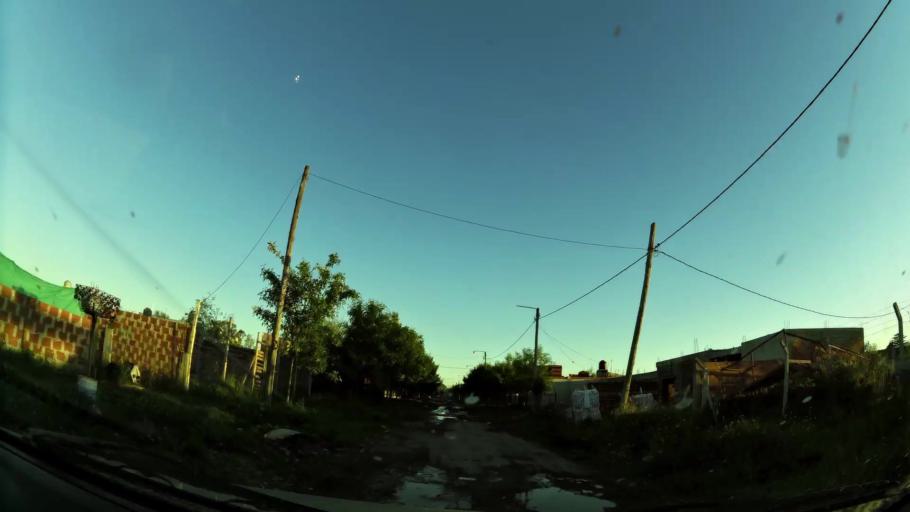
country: AR
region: Buenos Aires
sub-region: Partido de Almirante Brown
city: Adrogue
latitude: -34.7906
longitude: -58.3427
